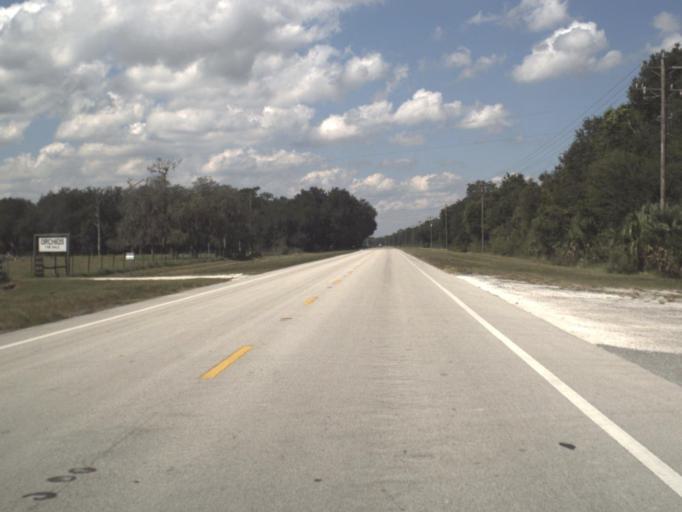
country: US
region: Florida
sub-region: Okeechobee County
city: Okeechobee
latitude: 27.3871
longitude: -81.0138
